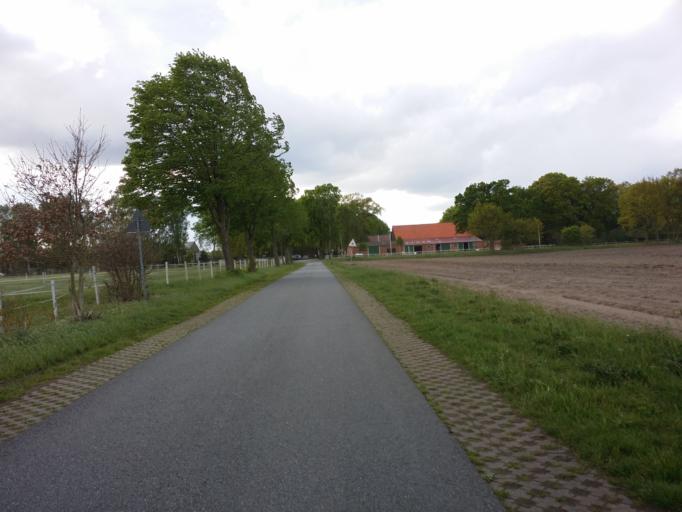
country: DE
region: Lower Saxony
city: Kirchseelte
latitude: 52.9869
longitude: 8.6819
